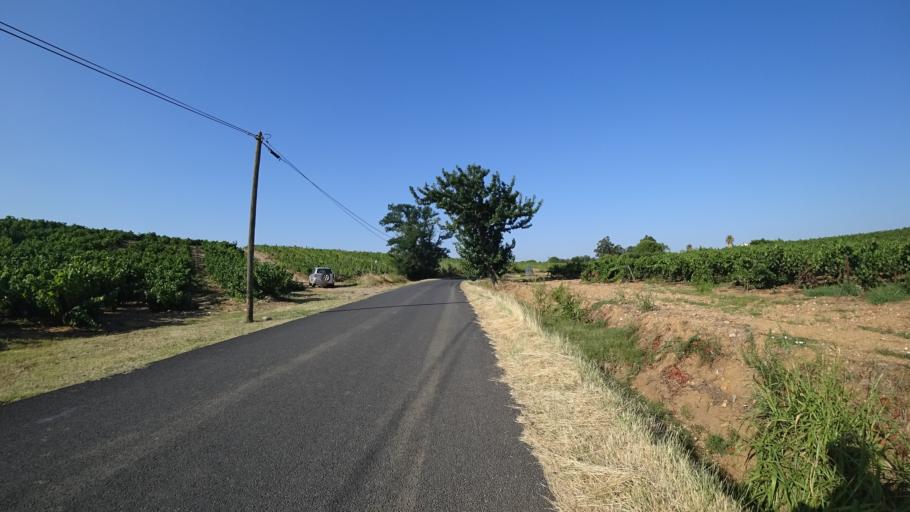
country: FR
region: Languedoc-Roussillon
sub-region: Departement des Pyrenees-Orientales
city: Villelongue-de-la-Salanque
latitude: 42.6972
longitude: 2.9832
